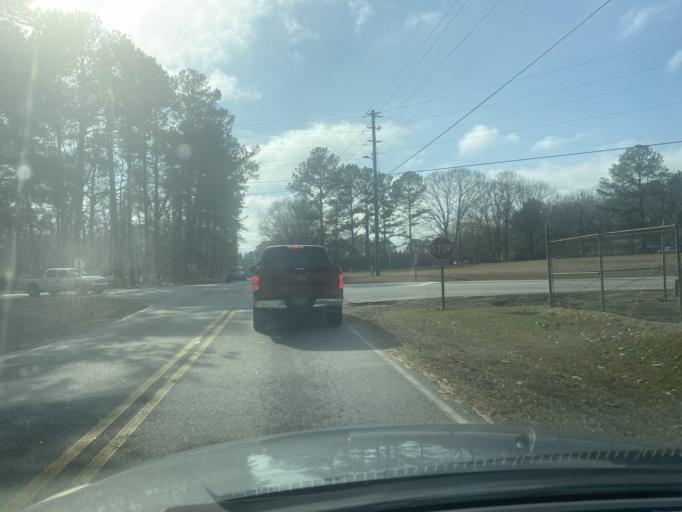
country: US
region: Georgia
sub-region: Henry County
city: Stockbridge
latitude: 33.4785
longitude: -84.2276
